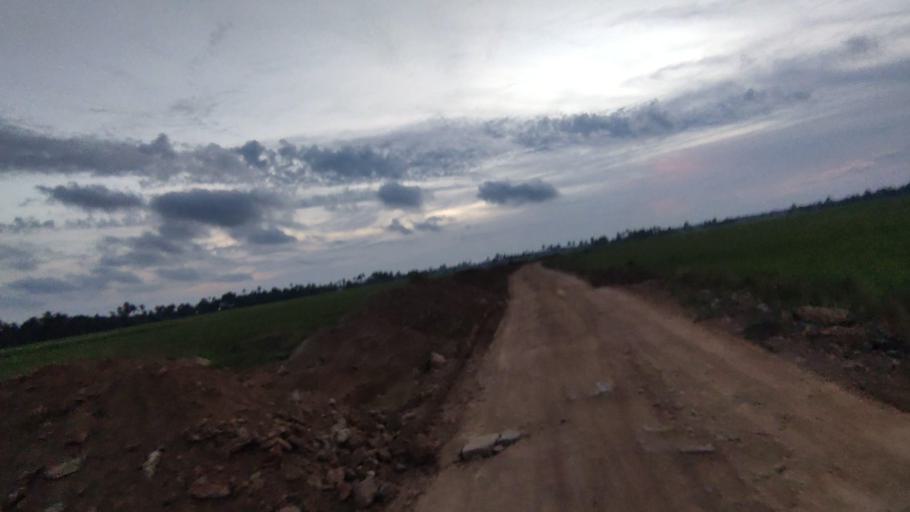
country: IN
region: Kerala
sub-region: Kottayam
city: Kottayam
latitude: 9.6435
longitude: 76.4464
